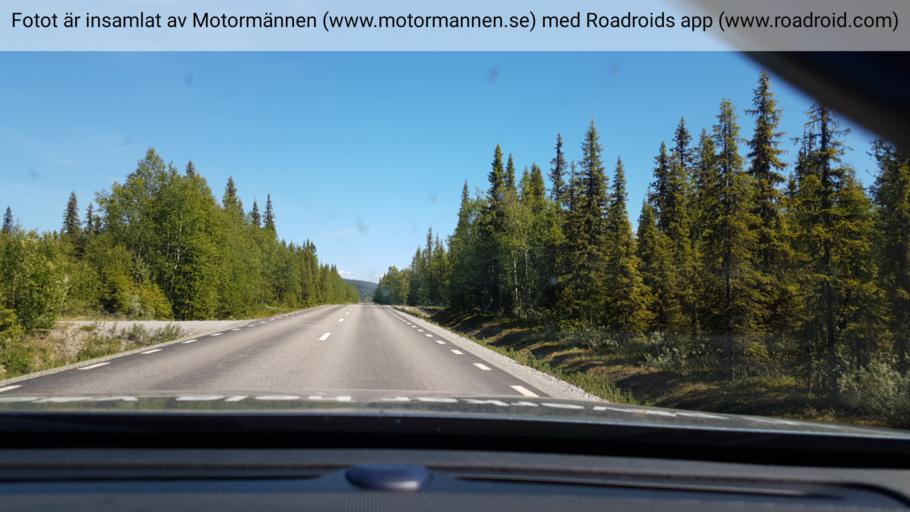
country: SE
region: Vaesterbotten
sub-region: Asele Kommun
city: Insjon
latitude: 64.7250
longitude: 17.5950
